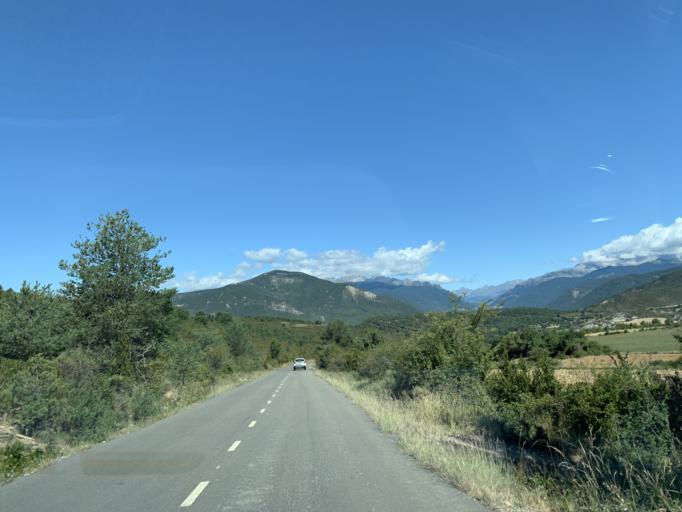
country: ES
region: Aragon
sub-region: Provincia de Huesca
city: Sabinanigo
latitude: 42.5223
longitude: -0.3231
